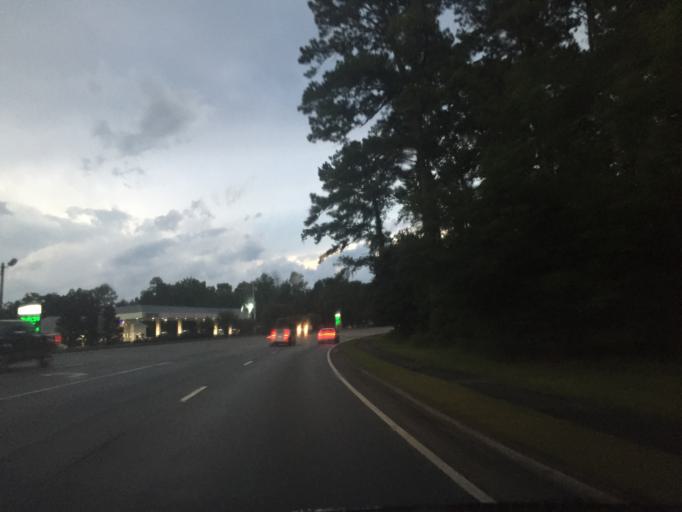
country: US
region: Georgia
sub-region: Liberty County
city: Hinesville
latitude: 31.8589
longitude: -81.5650
